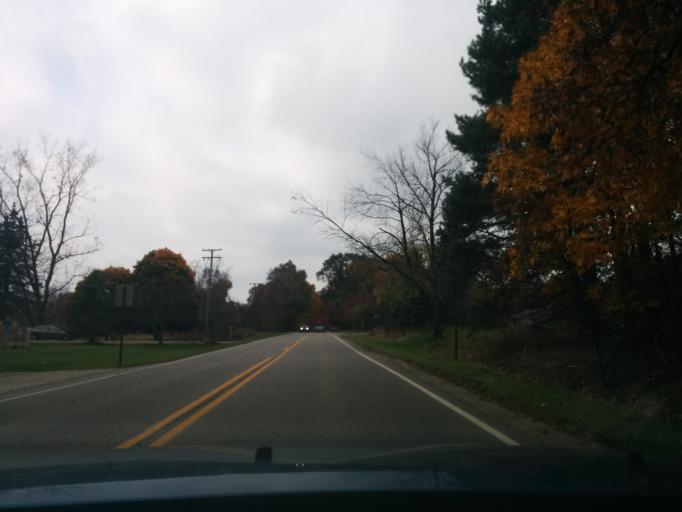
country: US
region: Michigan
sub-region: Washtenaw County
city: Dexter
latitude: 42.3881
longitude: -83.9234
